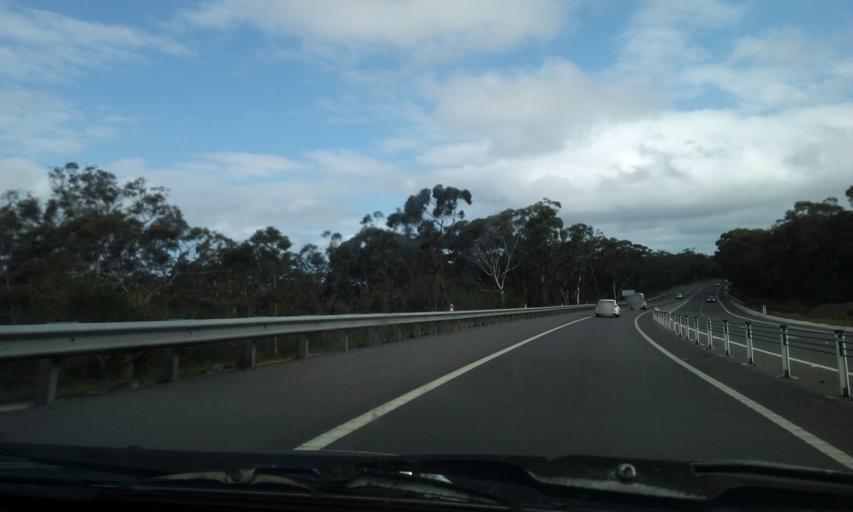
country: AU
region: New South Wales
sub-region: Wollongong
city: Bulli
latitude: -34.2687
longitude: 150.8958
